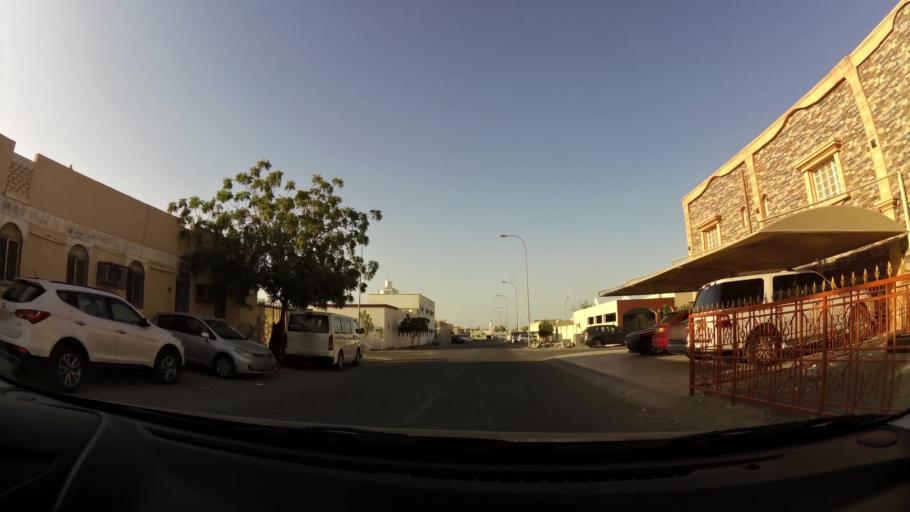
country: OM
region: Muhafazat Masqat
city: As Sib al Jadidah
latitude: 23.6258
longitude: 58.1920
